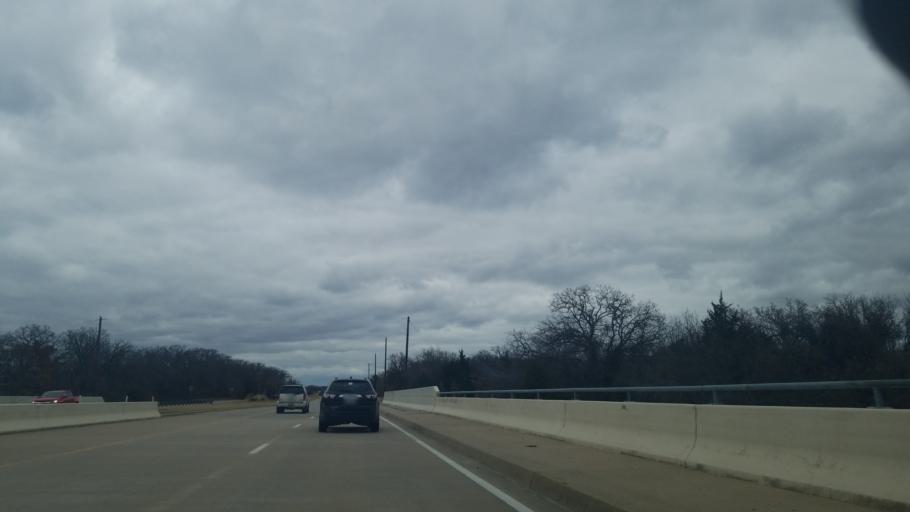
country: US
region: Texas
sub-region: Denton County
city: Copper Canyon
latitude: 33.1066
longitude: -97.0789
